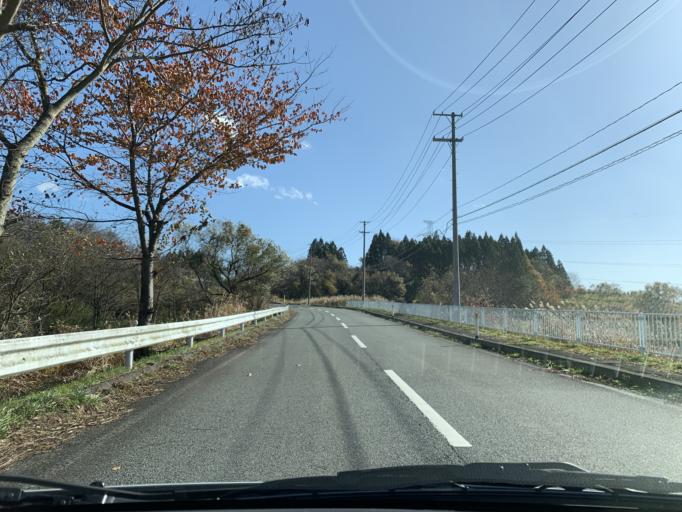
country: JP
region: Iwate
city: Mizusawa
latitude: 39.0279
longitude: 141.1111
